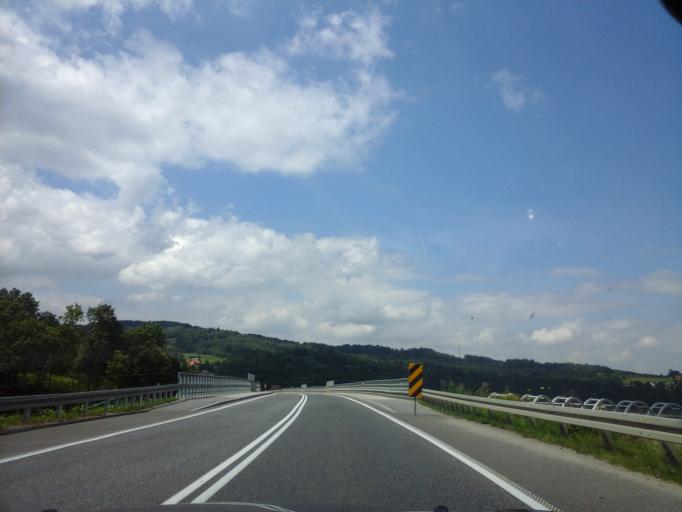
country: PL
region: Lesser Poland Voivodeship
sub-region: Powiat suski
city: Zembrzyce
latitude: 49.7800
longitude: 19.5880
